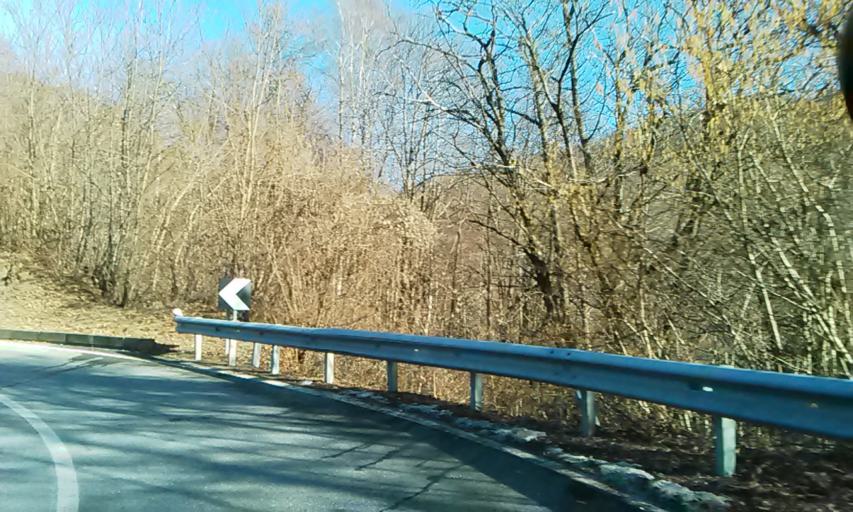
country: IT
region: Piedmont
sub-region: Provincia di Vercelli
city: Cellio
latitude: 45.7461
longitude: 8.3105
